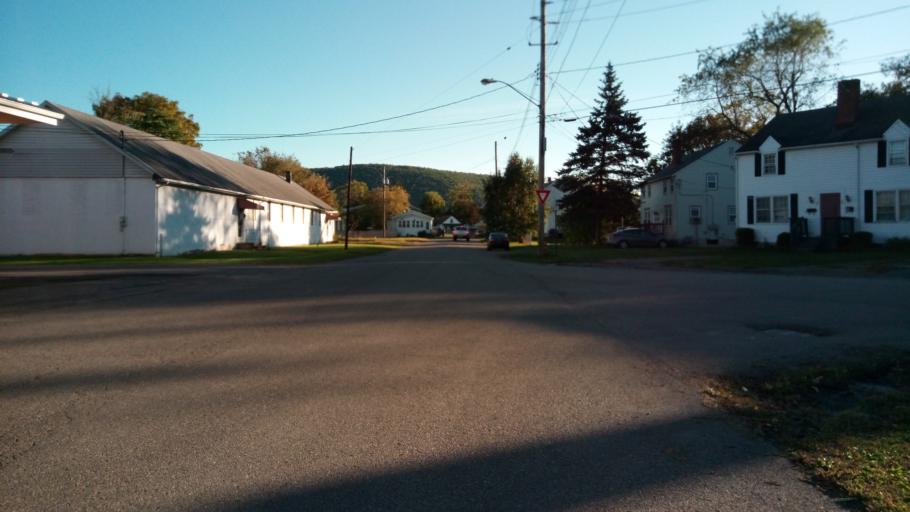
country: US
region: New York
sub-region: Chemung County
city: Southport
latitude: 42.0650
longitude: -76.8057
